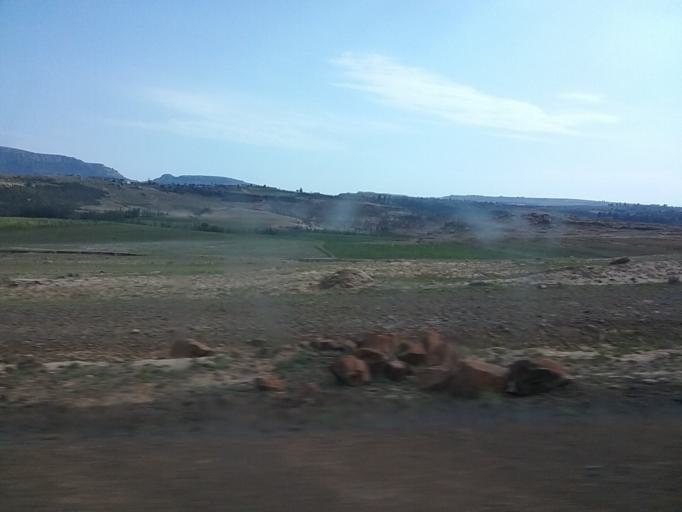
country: LS
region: Berea
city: Teyateyaneng
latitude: -29.0853
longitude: 27.9159
